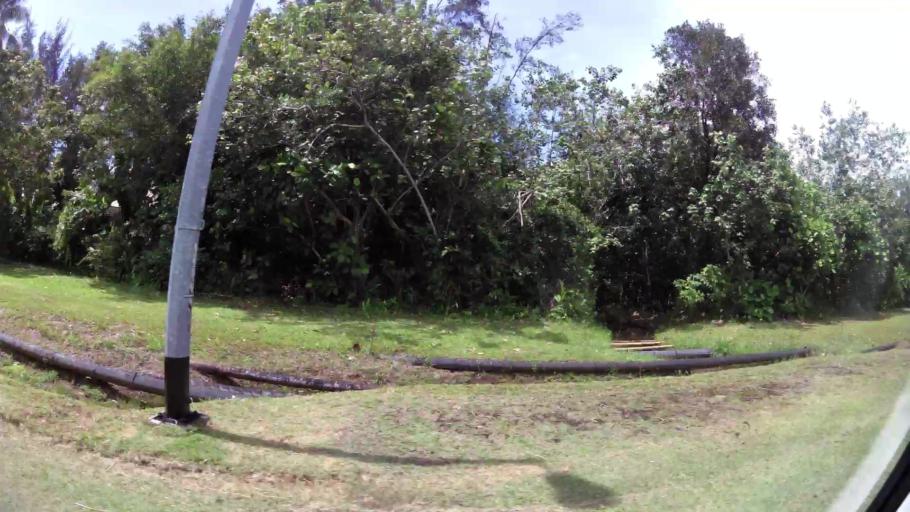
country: BN
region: Belait
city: Seria
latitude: 4.6031
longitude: 114.2806
